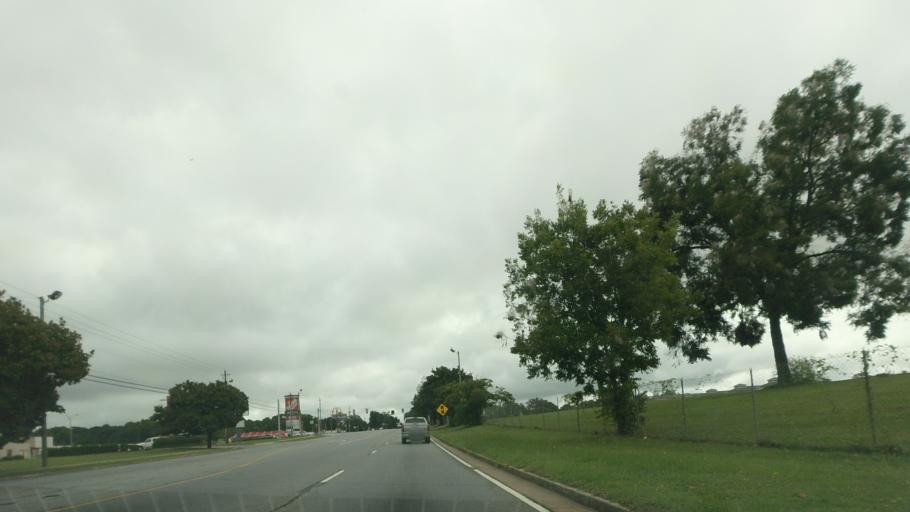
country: US
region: Georgia
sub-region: Laurens County
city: Dublin
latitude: 32.5403
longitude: -82.9458
